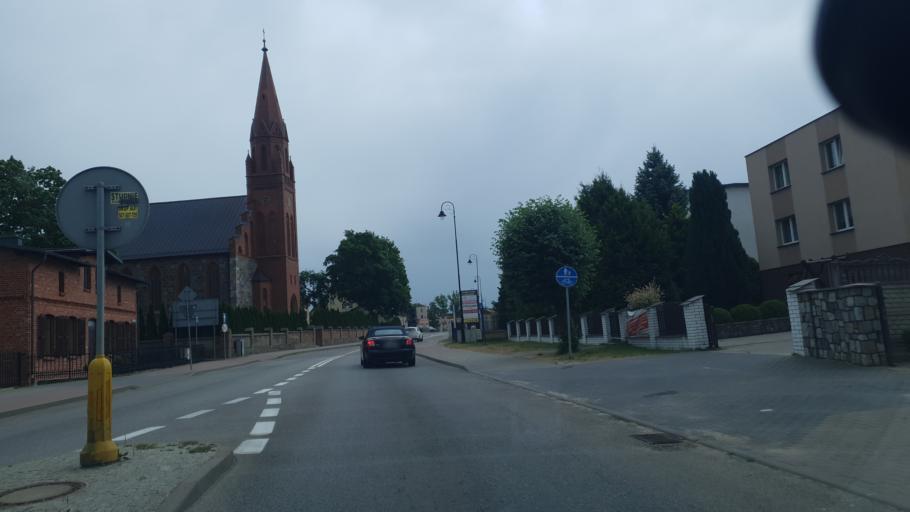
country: PL
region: Pomeranian Voivodeship
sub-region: Powiat kartuski
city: Przodkowo
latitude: 54.3794
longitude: 18.2876
